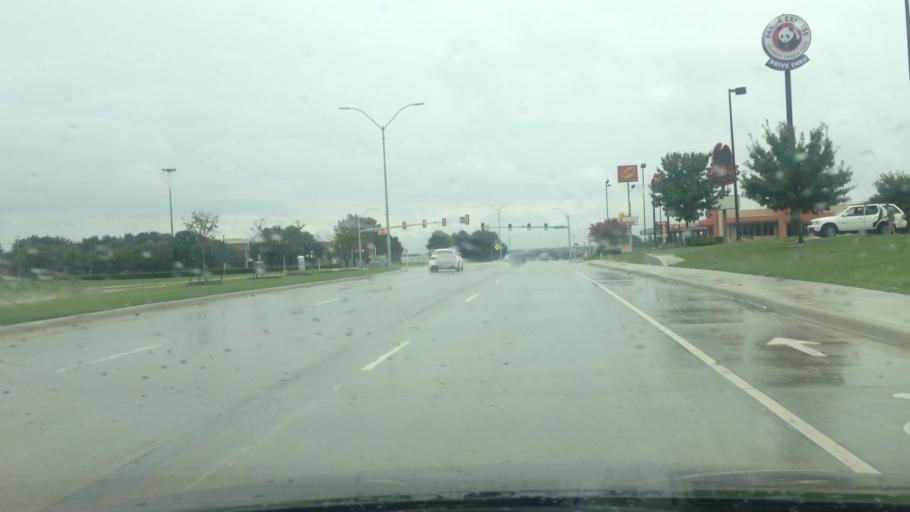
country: US
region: Texas
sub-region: Tarrant County
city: Watauga
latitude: 32.8422
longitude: -97.2904
